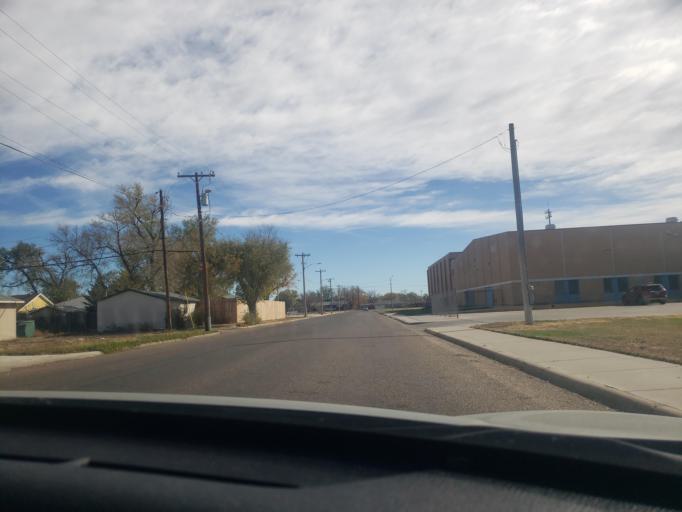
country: US
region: Kansas
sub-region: Finney County
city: Garden City
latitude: 37.9791
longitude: -100.8687
